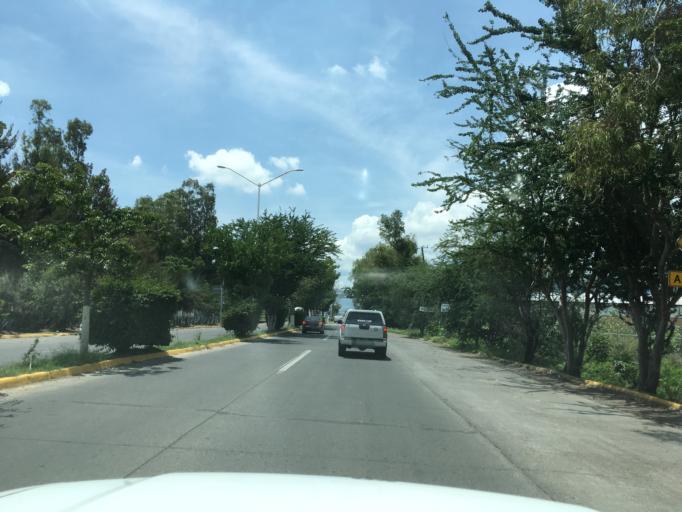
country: MX
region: Jalisco
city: Tlajomulco de Zuniga
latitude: 20.4634
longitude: -103.4466
